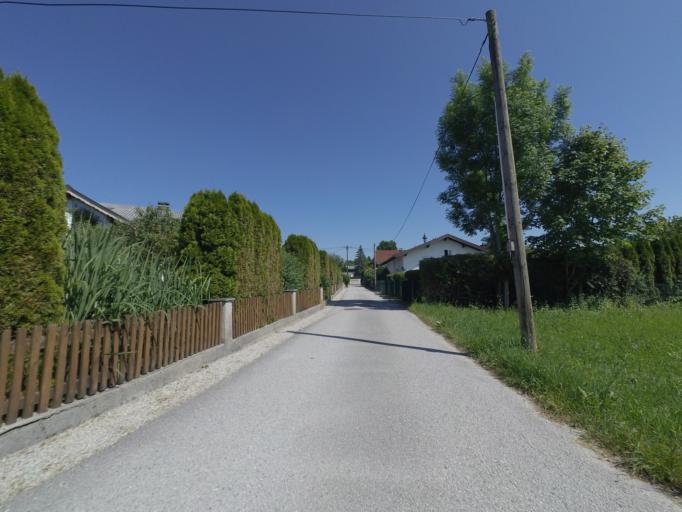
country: AT
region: Salzburg
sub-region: Politischer Bezirk Salzburg-Umgebung
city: Grodig
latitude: 47.7616
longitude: 13.0320
